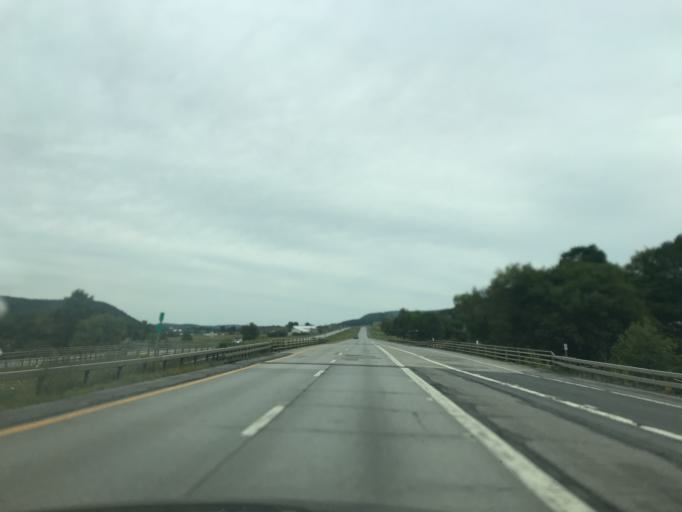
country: US
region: New York
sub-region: Schoharie County
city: Cobleskill
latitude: 42.6419
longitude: -74.5438
